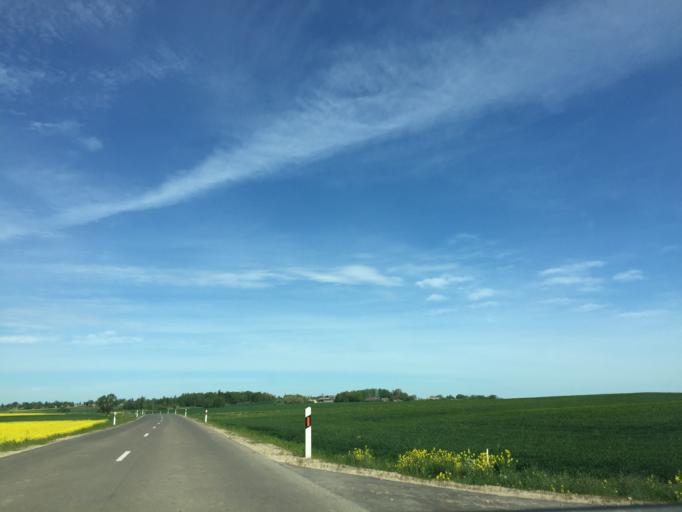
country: LT
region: Panevezys
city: Pasvalys
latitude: 56.1103
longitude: 24.2449
